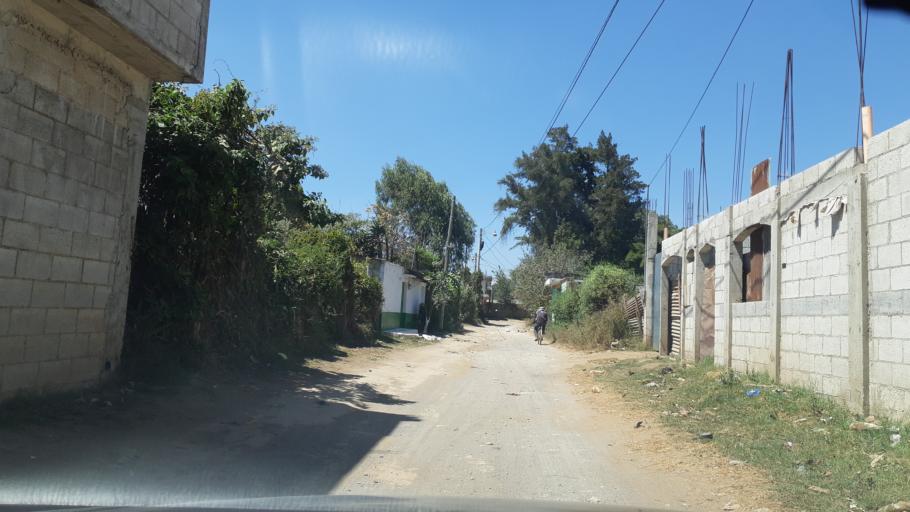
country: GT
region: Chimaltenango
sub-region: Municipio de Chimaltenango
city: Chimaltenango
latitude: 14.6491
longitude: -90.8106
